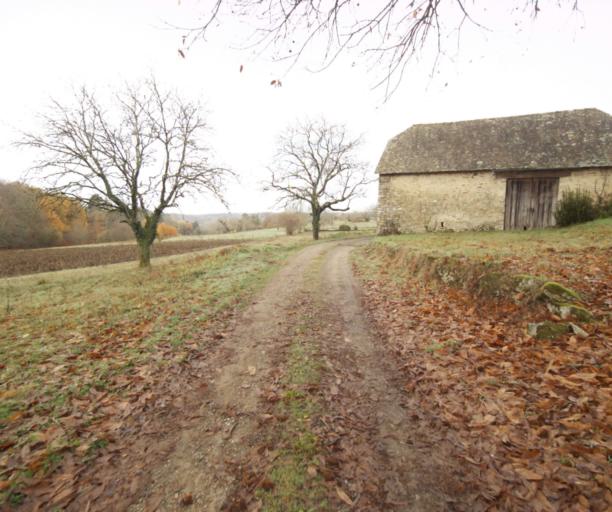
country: FR
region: Limousin
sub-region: Departement de la Correze
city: Cornil
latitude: 45.2033
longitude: 1.7200
